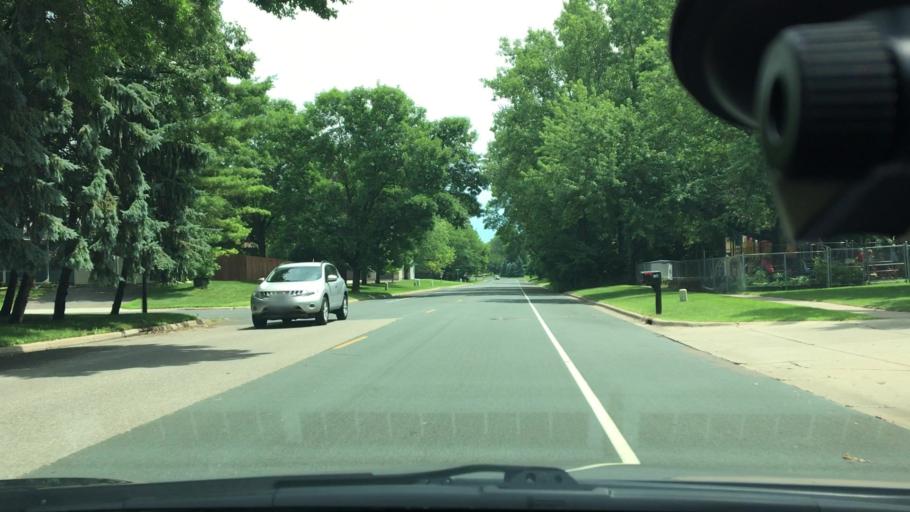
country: US
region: Minnesota
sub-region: Hennepin County
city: Maple Grove
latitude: 45.0675
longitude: -93.4383
